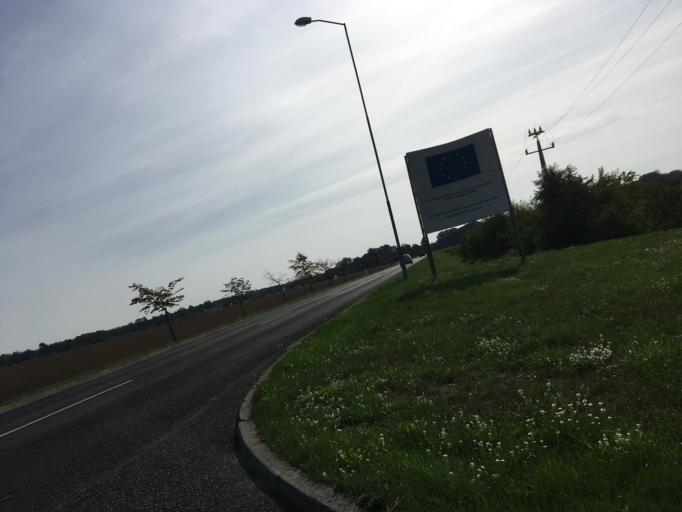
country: DE
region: Brandenburg
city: Forst
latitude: 51.7635
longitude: 14.6571
